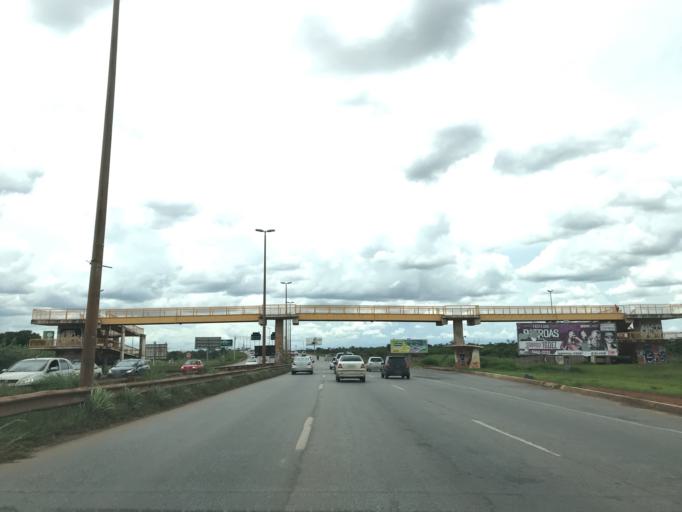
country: BR
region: Federal District
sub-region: Brasilia
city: Brasilia
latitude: -15.7867
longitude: -47.9458
